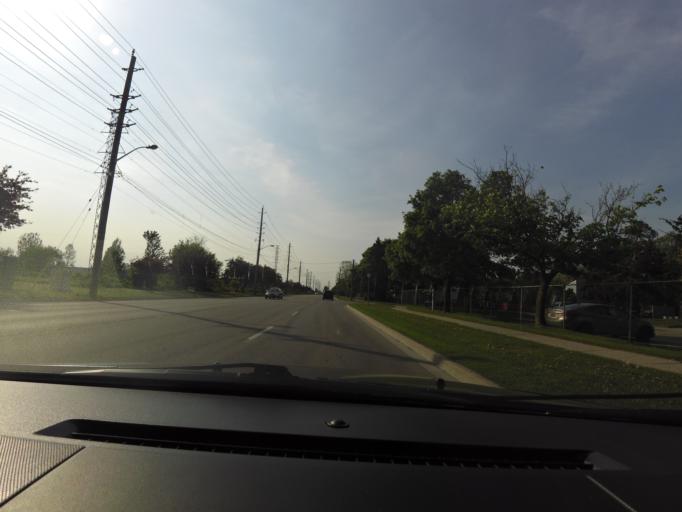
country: CA
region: Ontario
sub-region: Wellington County
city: Guelph
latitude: 43.5552
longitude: -80.2829
